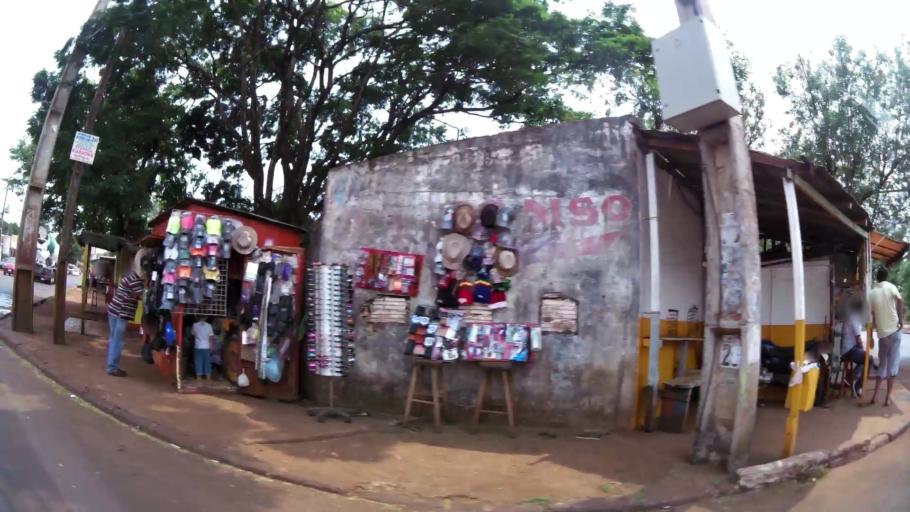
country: PY
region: Alto Parana
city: Presidente Franco
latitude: -25.5540
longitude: -54.6296
